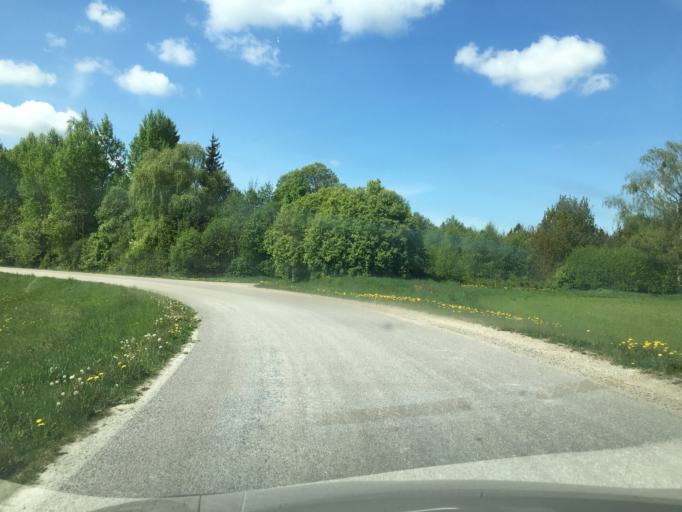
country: EE
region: Harju
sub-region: Saue linn
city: Saue
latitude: 59.2917
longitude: 24.5046
